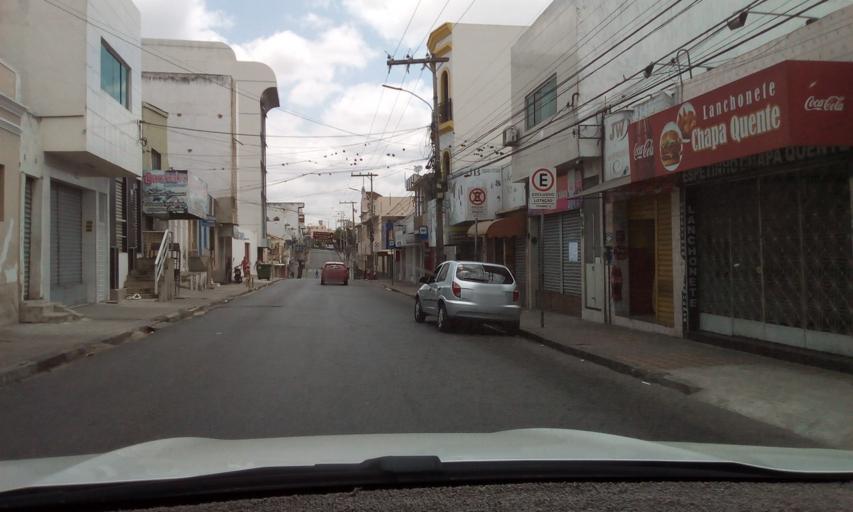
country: BR
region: Pernambuco
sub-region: Caruaru
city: Caruaru
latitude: -8.2876
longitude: -35.9742
